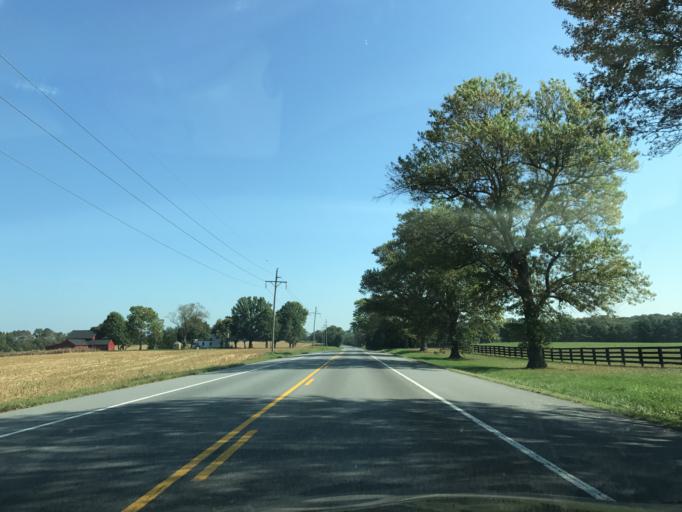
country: US
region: Maryland
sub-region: Queen Anne's County
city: Kingstown
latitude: 39.2479
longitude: -76.0151
